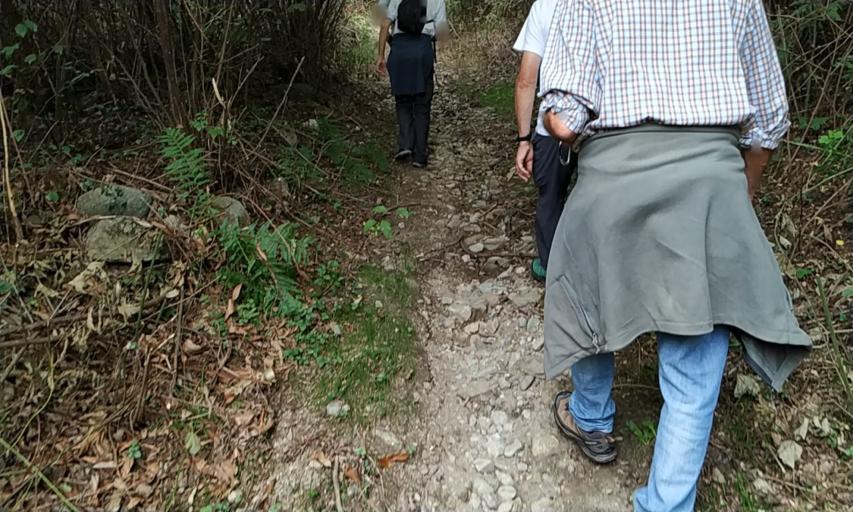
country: IT
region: Piedmont
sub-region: Provincia di Biella
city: Dorzano
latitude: 45.4315
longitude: 8.0874
